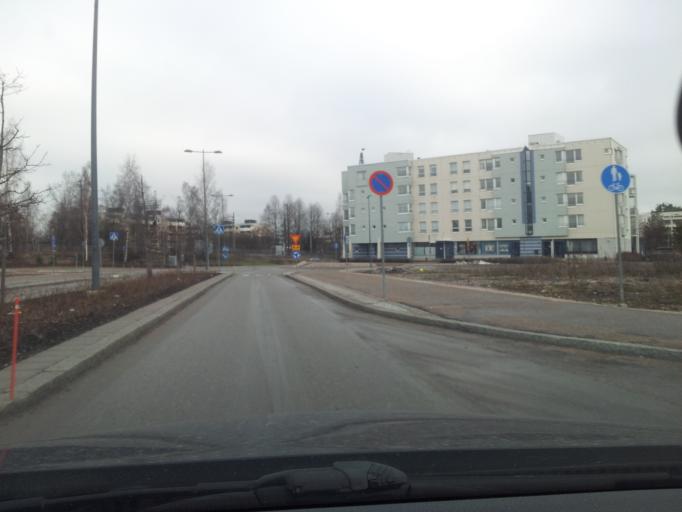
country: FI
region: Uusimaa
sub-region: Helsinki
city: Espoo
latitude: 60.2055
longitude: 24.6637
